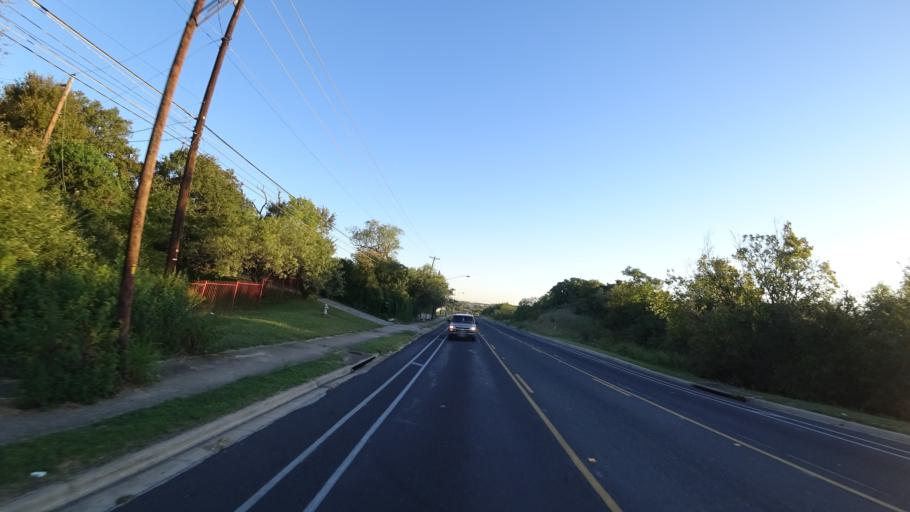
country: US
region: Texas
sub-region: Travis County
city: Austin
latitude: 30.3015
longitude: -97.6727
